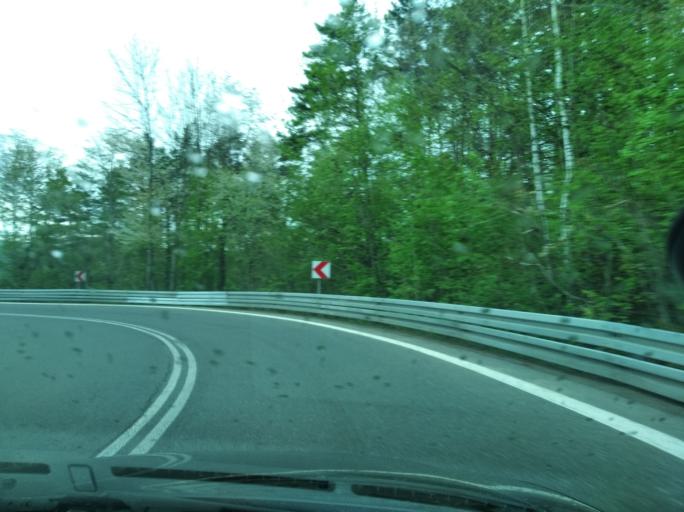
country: PL
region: Subcarpathian Voivodeship
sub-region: Powiat sanocki
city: Tyrawa Woloska
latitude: 49.5543
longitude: 22.3216
